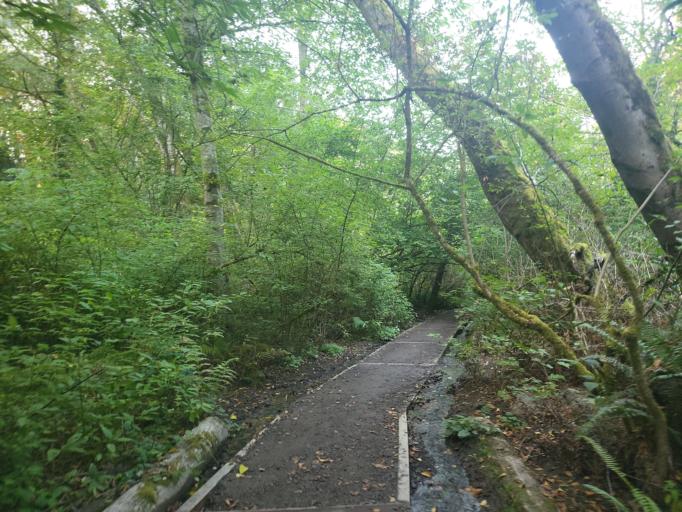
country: US
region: Washington
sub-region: Pierce County
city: Tacoma
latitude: 47.3166
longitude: -122.4144
